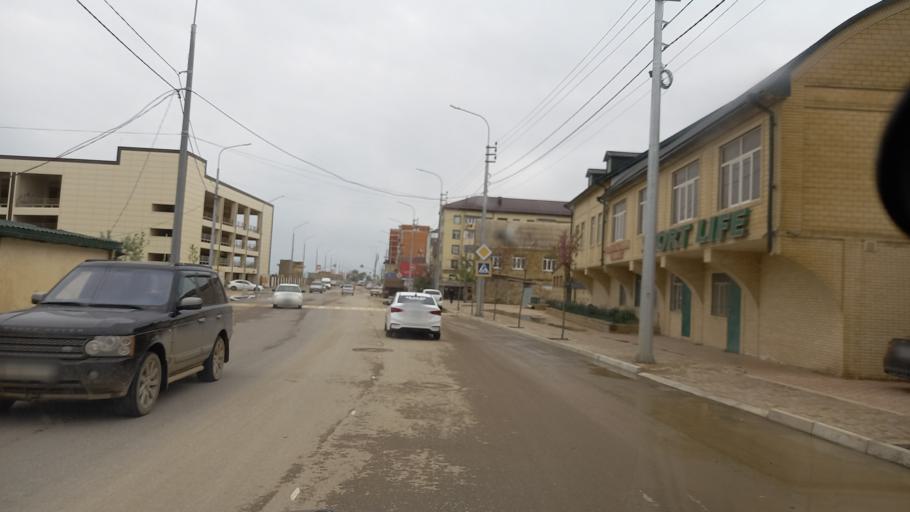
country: RU
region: Dagestan
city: Derbent
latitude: 42.0905
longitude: 48.2892
